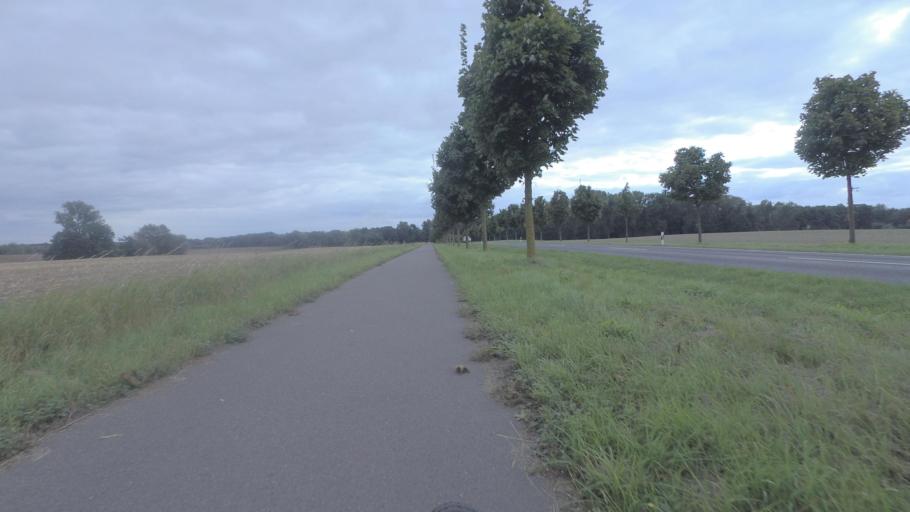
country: DE
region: Brandenburg
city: Werneuchen
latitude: 52.6033
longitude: 13.6859
